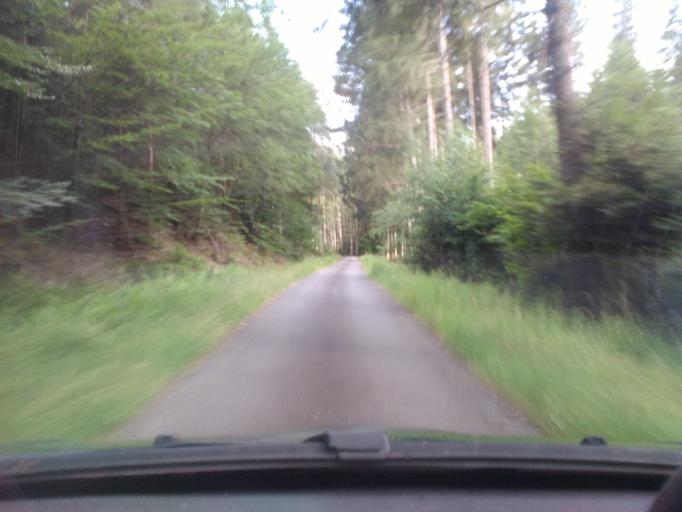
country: FR
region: Lorraine
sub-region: Departement des Vosges
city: Taintrux
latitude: 48.2387
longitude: 6.8146
